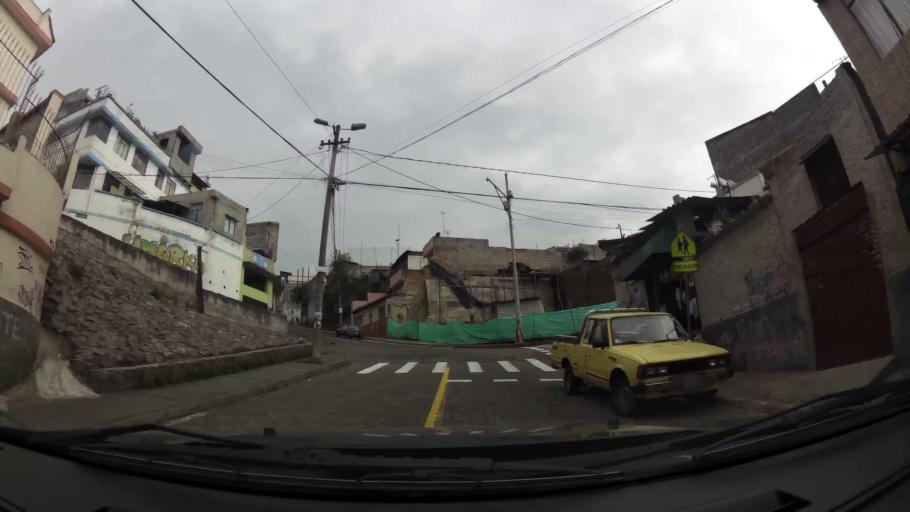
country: EC
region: Pichincha
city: Quito
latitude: -0.2127
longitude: -78.5106
